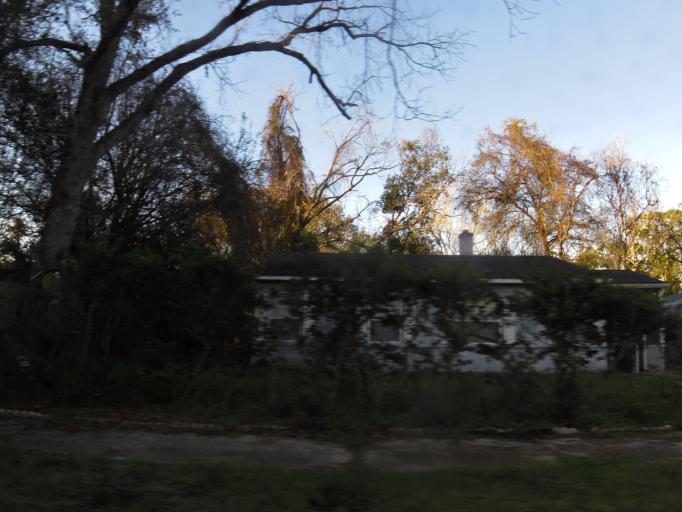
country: US
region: Florida
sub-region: Duval County
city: Jacksonville
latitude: 30.3353
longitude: -81.7094
